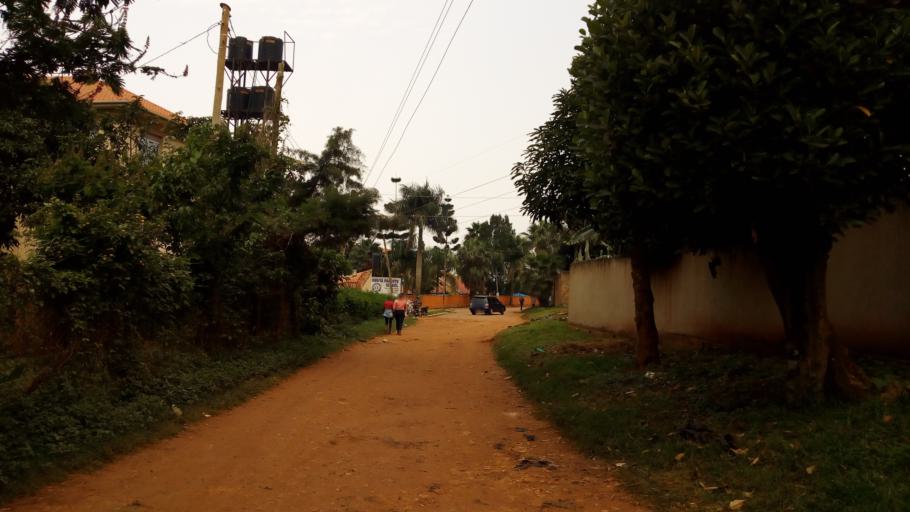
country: UG
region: Central Region
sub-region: Wakiso District
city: Kireka
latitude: 0.3281
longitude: 32.6351
